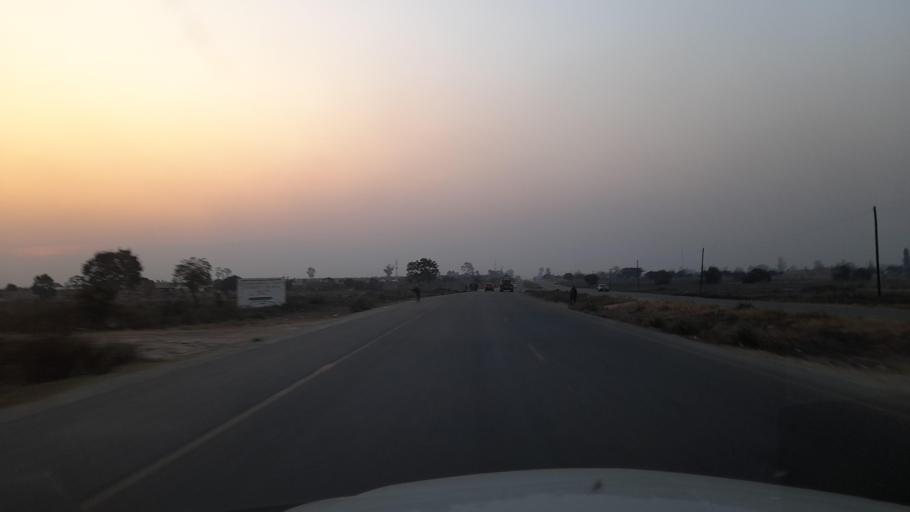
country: ZM
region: Copperbelt
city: Kitwe
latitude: -12.7611
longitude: 28.1673
